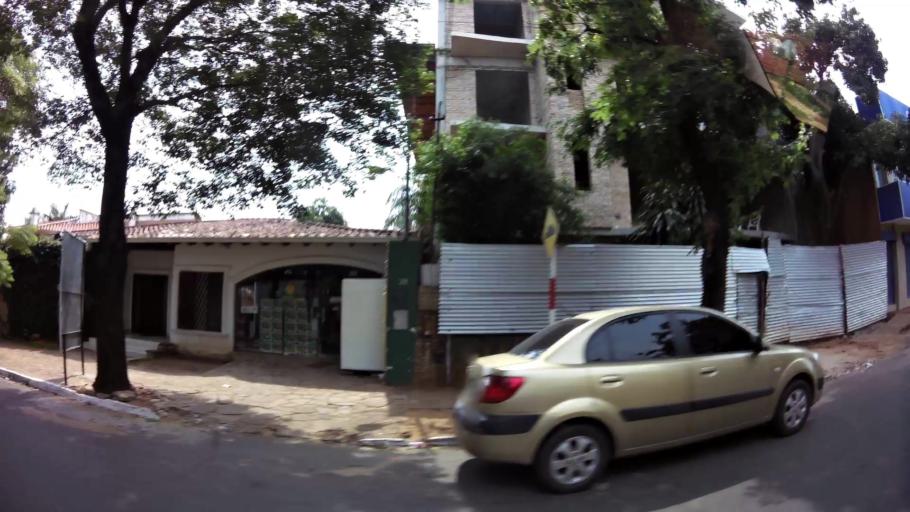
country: PY
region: Asuncion
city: Asuncion
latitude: -25.2748
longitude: -57.5645
